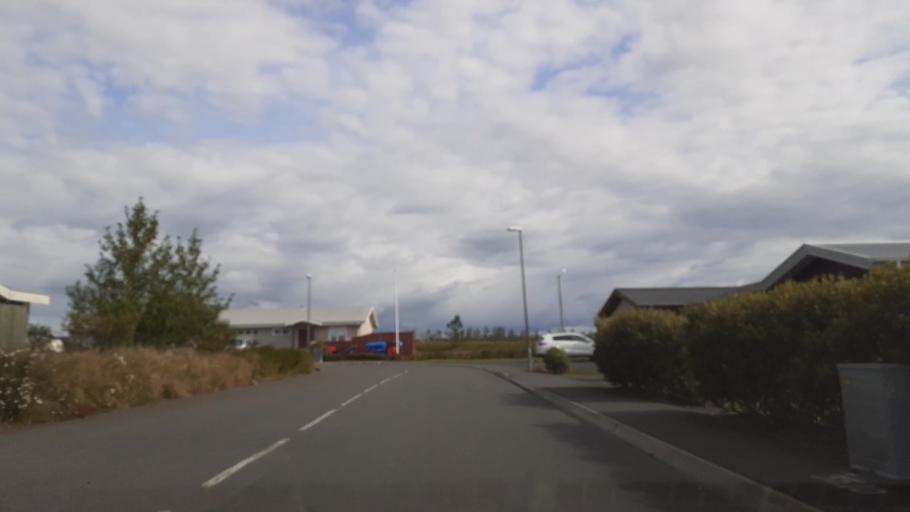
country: IS
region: South
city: Vestmannaeyjar
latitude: 63.8335
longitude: -20.3867
